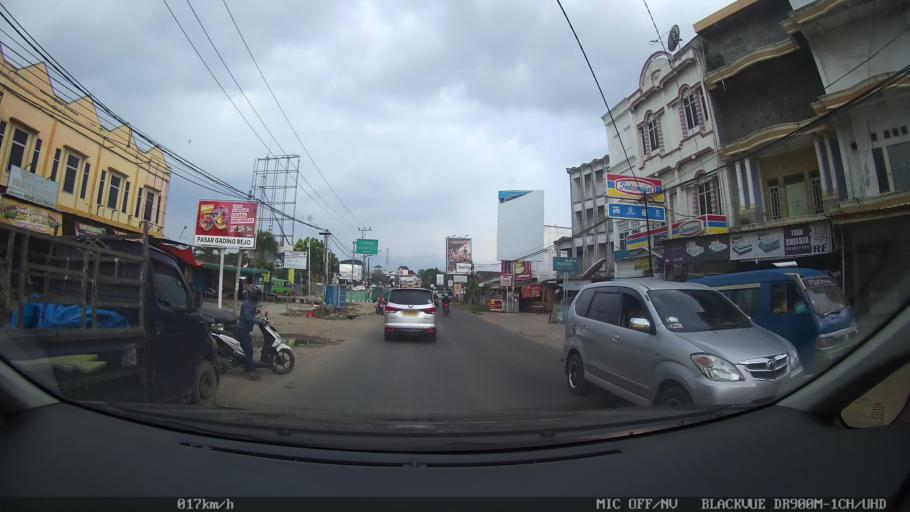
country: ID
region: Lampung
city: Gadingrejo
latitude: -5.3739
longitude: 105.0607
